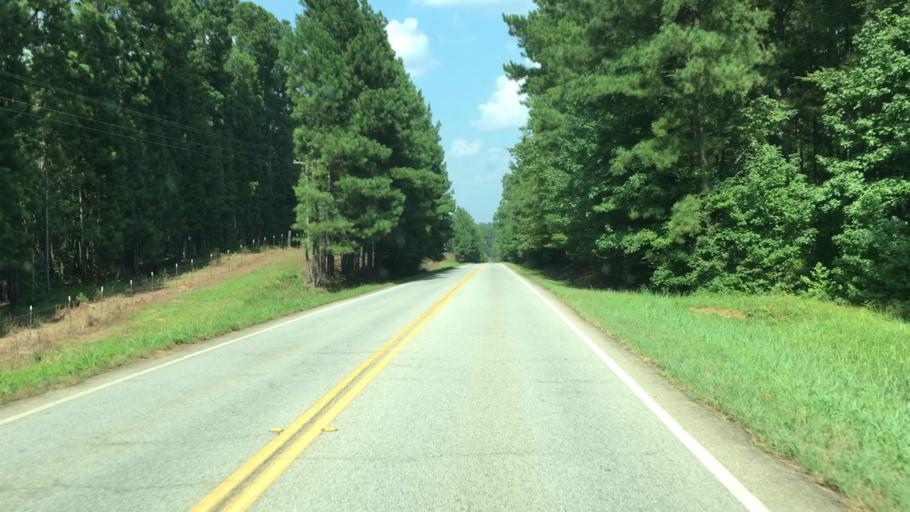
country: US
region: Georgia
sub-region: Butts County
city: Indian Springs
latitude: 33.1359
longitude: -83.8635
